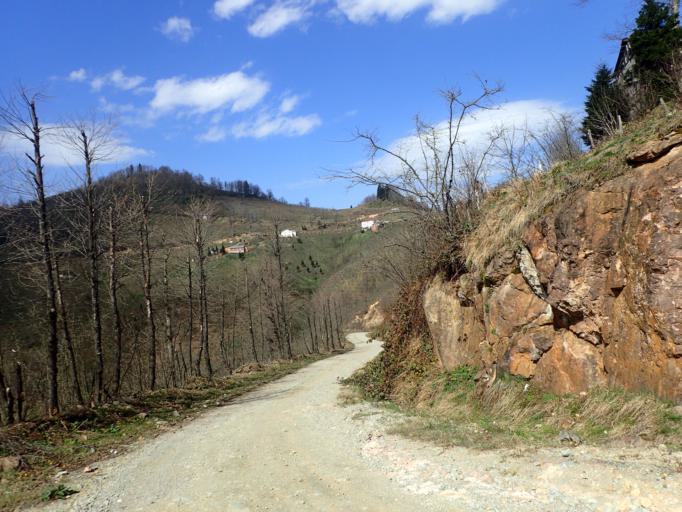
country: TR
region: Ordu
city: Kabaduz
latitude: 40.8167
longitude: 37.9043
